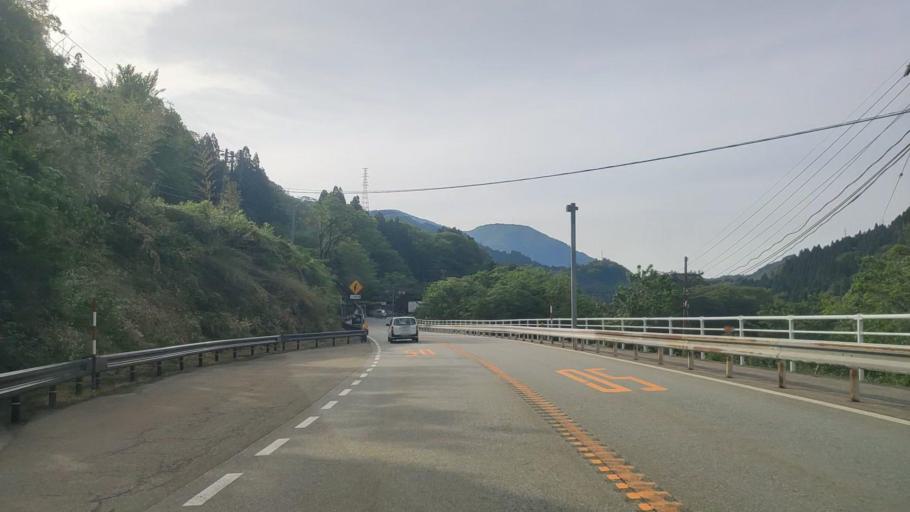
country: JP
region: Toyama
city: Yatsuomachi-higashikumisaka
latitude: 36.4546
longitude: 137.2531
